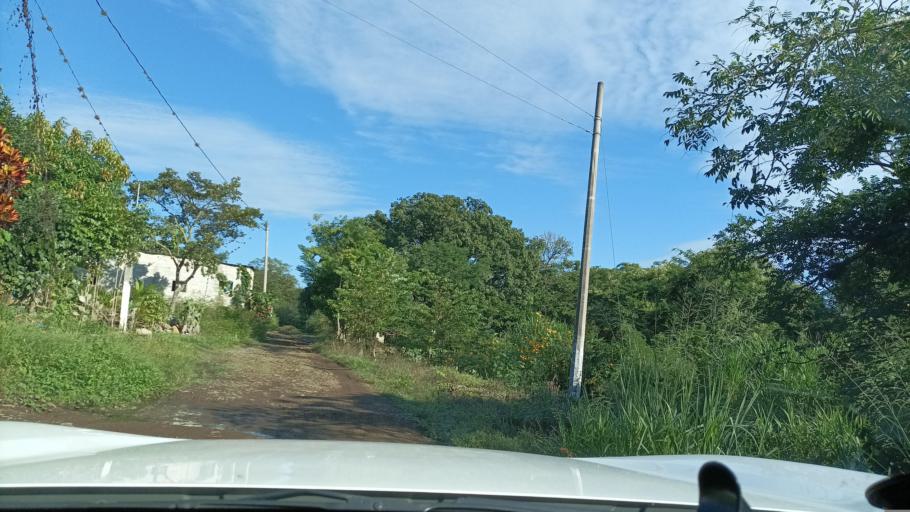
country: MX
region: Veracruz
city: Paso del Macho
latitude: 18.9765
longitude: -96.7307
